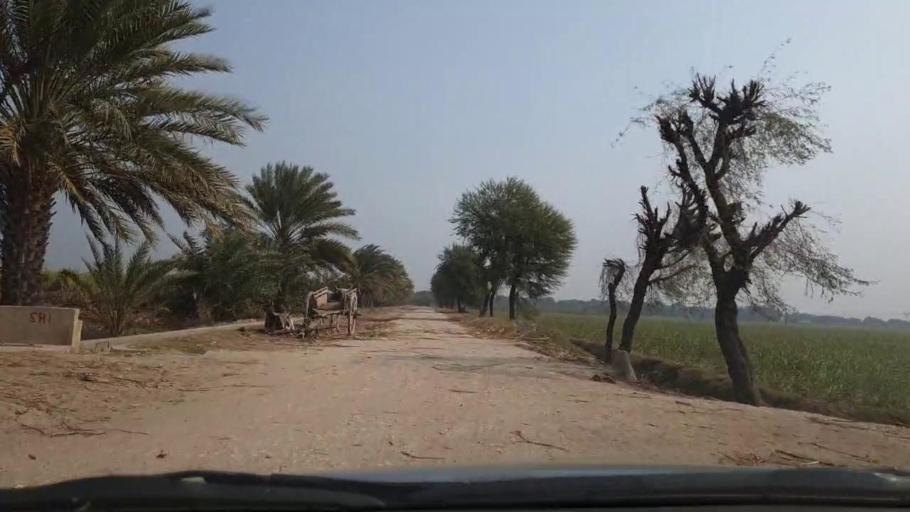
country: PK
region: Sindh
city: Matiari
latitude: 25.6573
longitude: 68.5306
